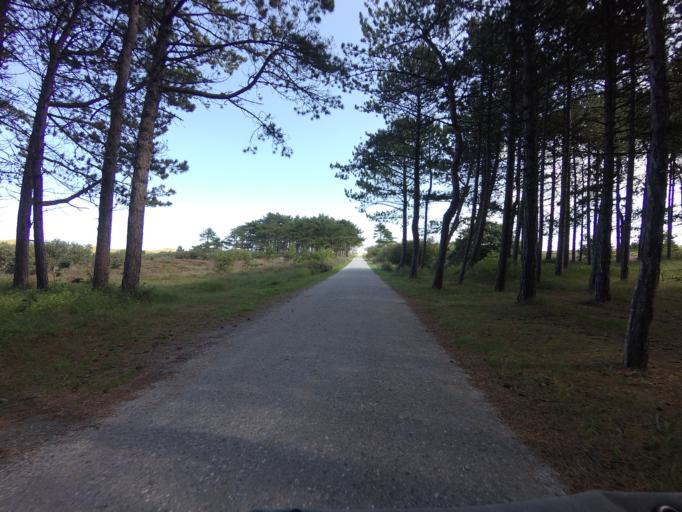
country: NL
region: Friesland
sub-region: Gemeente Terschelling
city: West-Terschelling
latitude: 53.3911
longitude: 5.2343
